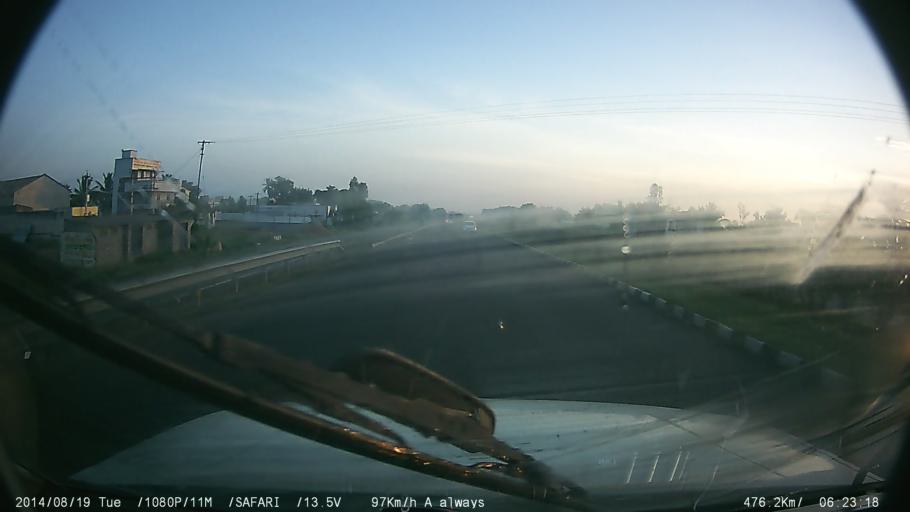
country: IN
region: Tamil Nadu
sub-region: Dharmapuri
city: Dharmapuri
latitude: 12.0371
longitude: 78.1031
